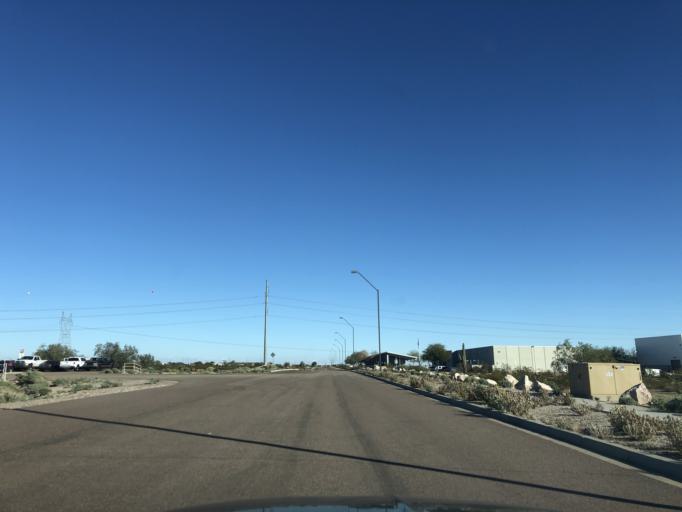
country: US
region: Arizona
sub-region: Maricopa County
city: Buckeye
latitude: 33.4281
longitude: -112.6027
